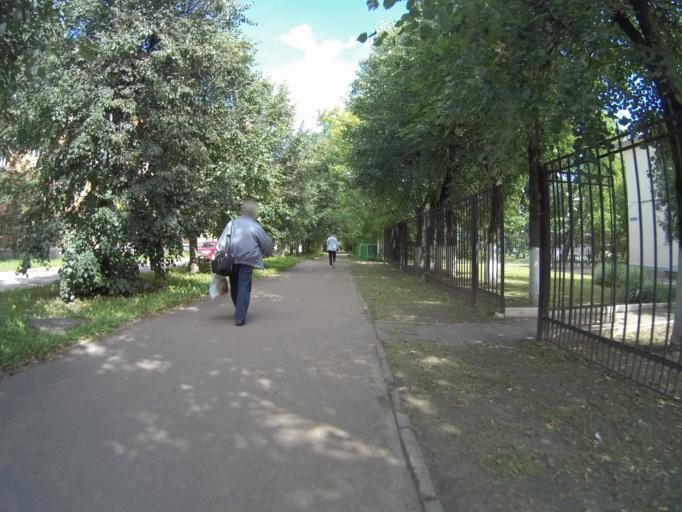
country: RU
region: Vladimir
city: Vladimir
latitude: 56.1400
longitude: 40.4186
